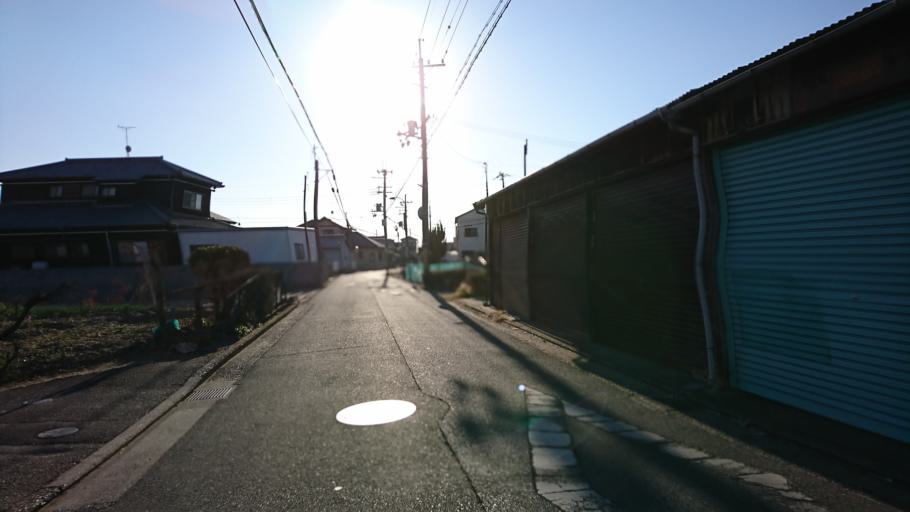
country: JP
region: Hyogo
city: Kakogawacho-honmachi
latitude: 34.7374
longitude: 134.8307
